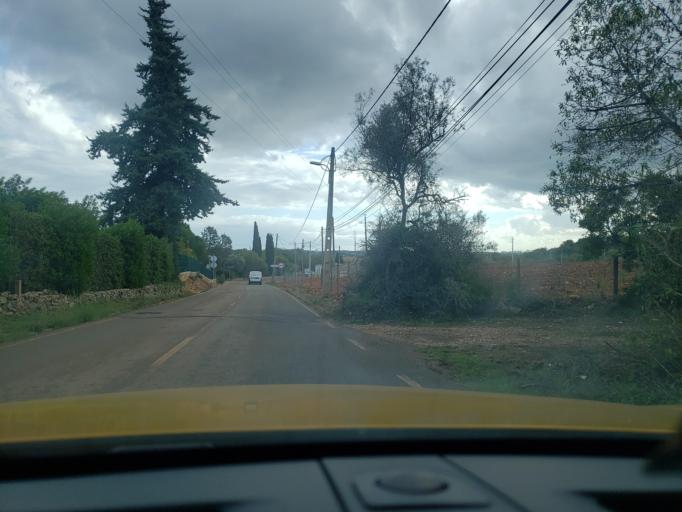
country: PT
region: Faro
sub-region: Portimao
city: Alvor
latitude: 37.1832
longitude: -8.5848
